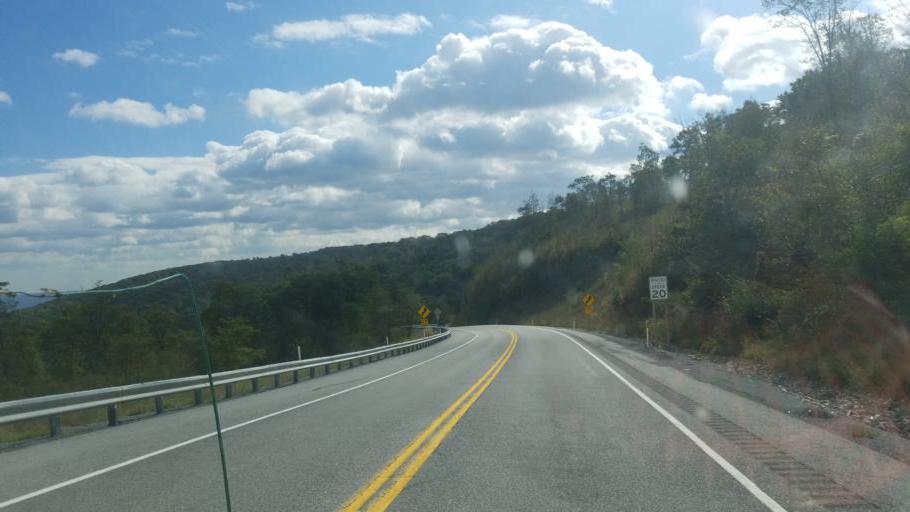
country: US
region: Pennsylvania
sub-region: Fulton County
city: McConnellsburg
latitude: 40.0165
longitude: -78.1489
